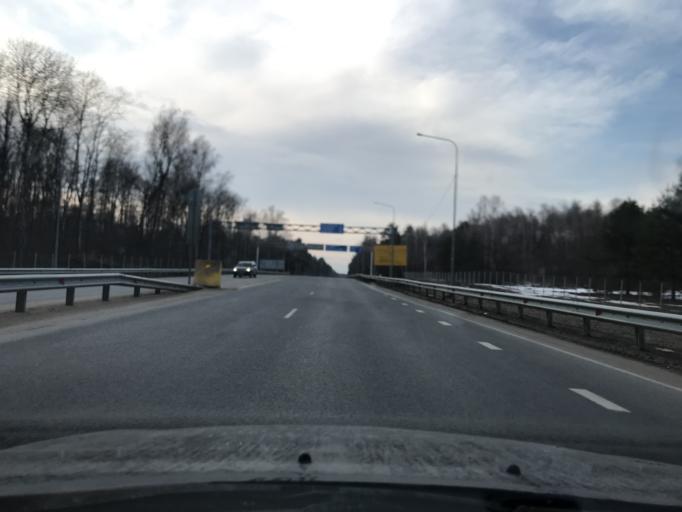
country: RU
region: Kaluga
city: Mstikhino
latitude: 54.5883
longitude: 36.0677
